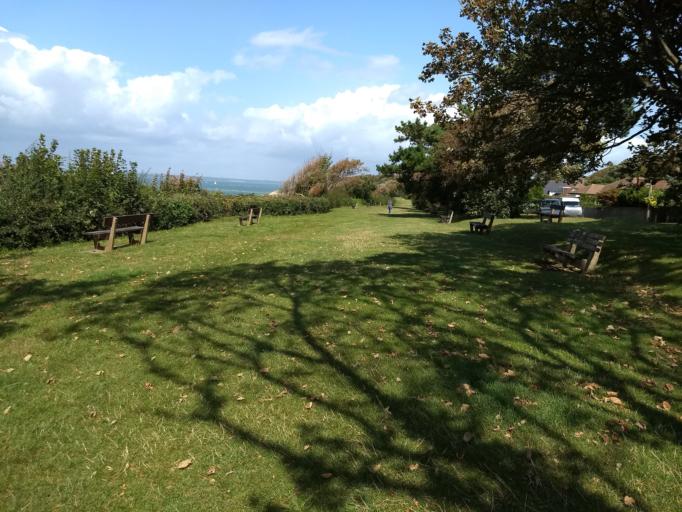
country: GB
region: England
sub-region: Isle of Wight
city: Totland
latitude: 50.6793
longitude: -1.5462
